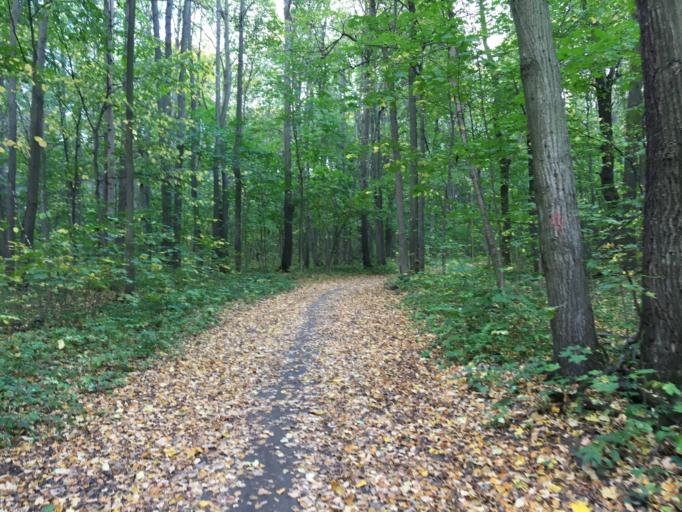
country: RU
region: Nizjnij Novgorod
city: Nizhniy Novgorod
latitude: 56.2684
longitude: 44.0092
